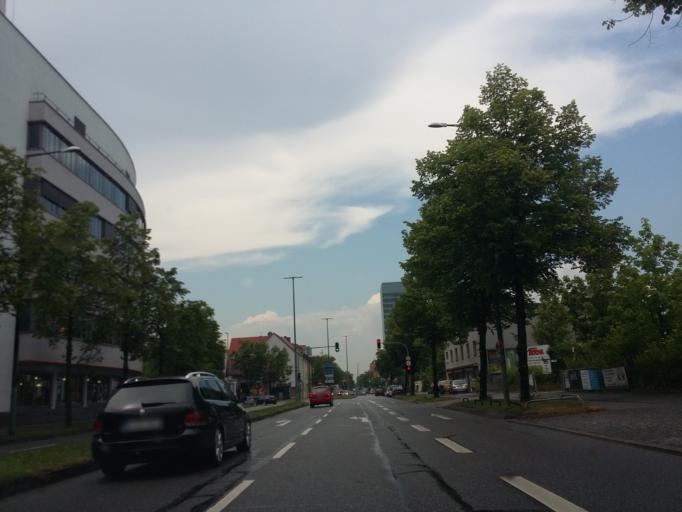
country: DE
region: Bavaria
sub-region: Upper Bavaria
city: Munich
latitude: 48.1296
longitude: 11.5330
